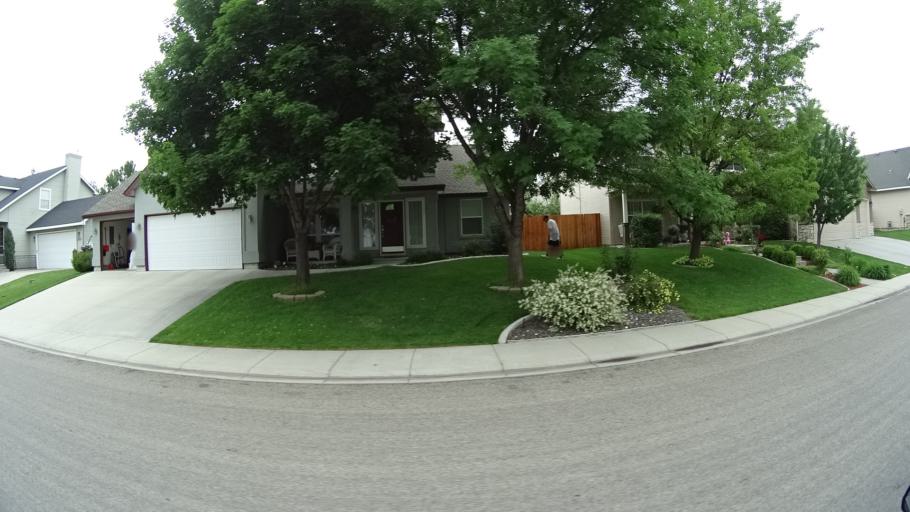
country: US
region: Idaho
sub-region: Ada County
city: Meridian
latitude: 43.5843
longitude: -116.3249
